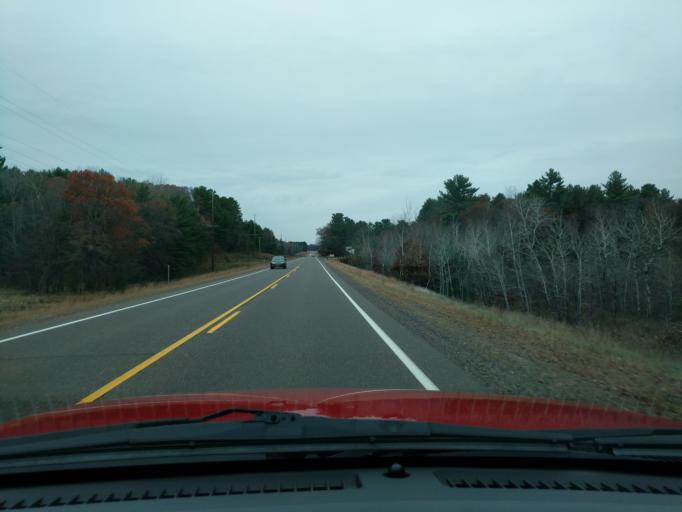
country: US
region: Wisconsin
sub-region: Burnett County
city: Siren
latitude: 45.8100
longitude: -92.2220
